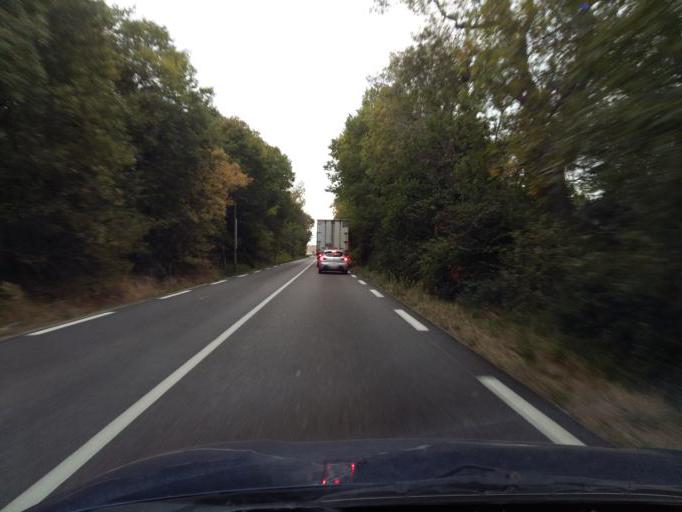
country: FR
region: Provence-Alpes-Cote d'Azur
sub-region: Departement des Bouches-du-Rhone
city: Miramas
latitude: 43.6112
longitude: 5.0110
